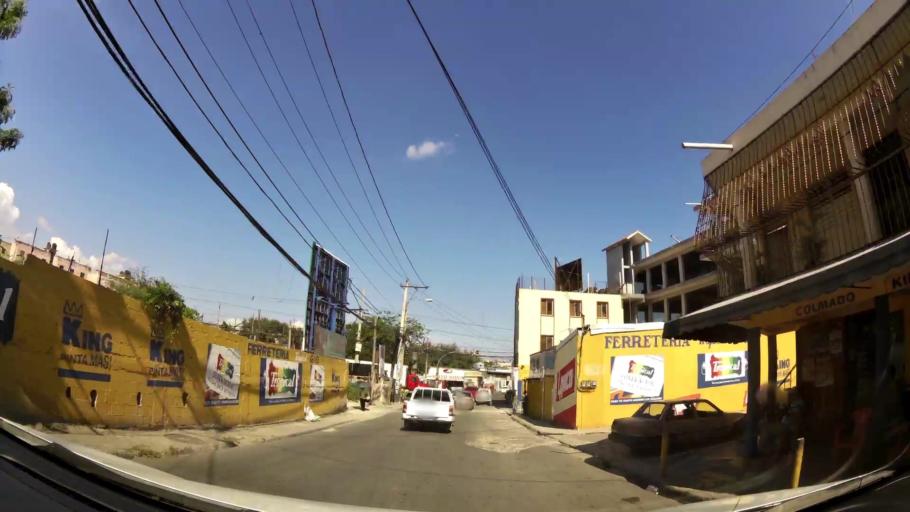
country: DO
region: Santo Domingo
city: Santo Domingo Oeste
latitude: 18.4646
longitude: -69.9946
